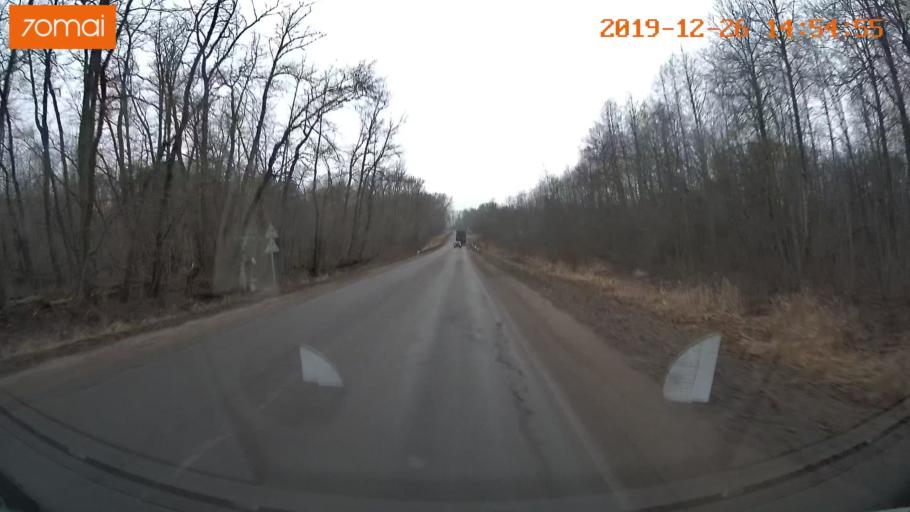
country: RU
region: Jaroslavl
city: Rybinsk
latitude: 58.3042
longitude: 38.8801
